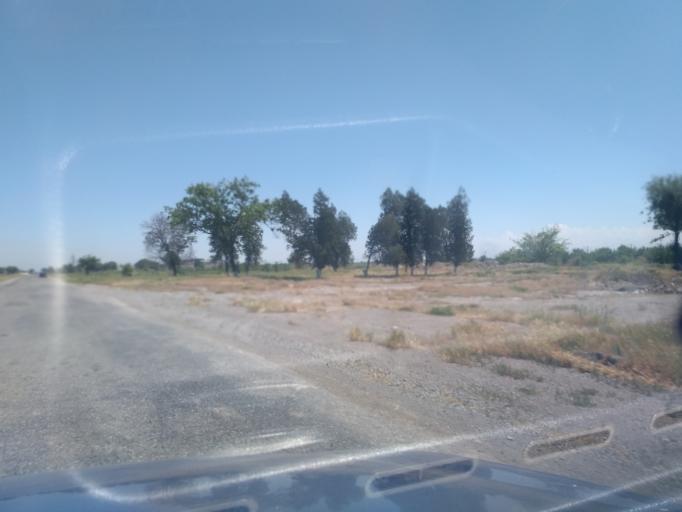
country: TJ
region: Viloyati Sughd
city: Zafarobod
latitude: 40.2156
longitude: 68.8790
